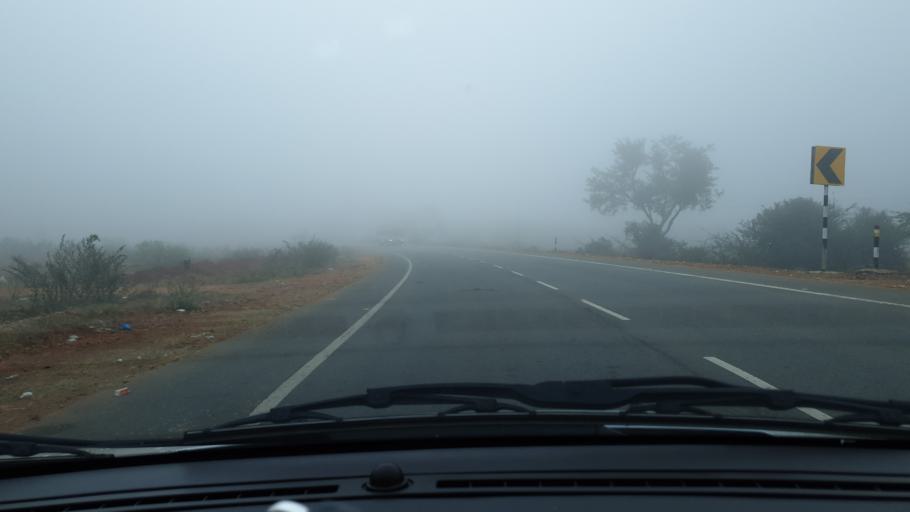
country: IN
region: Telangana
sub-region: Mahbubnagar
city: Nagar Karnul
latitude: 16.6512
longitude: 78.5761
